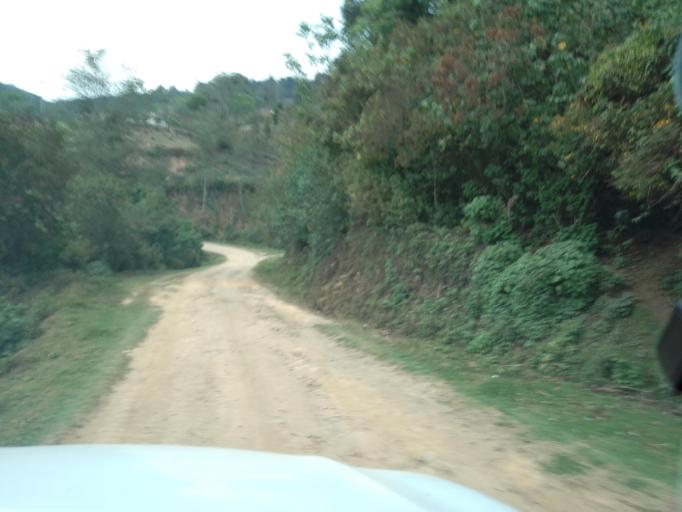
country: MX
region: Chiapas
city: Motozintla de Mendoza
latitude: 15.2163
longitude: -92.2317
